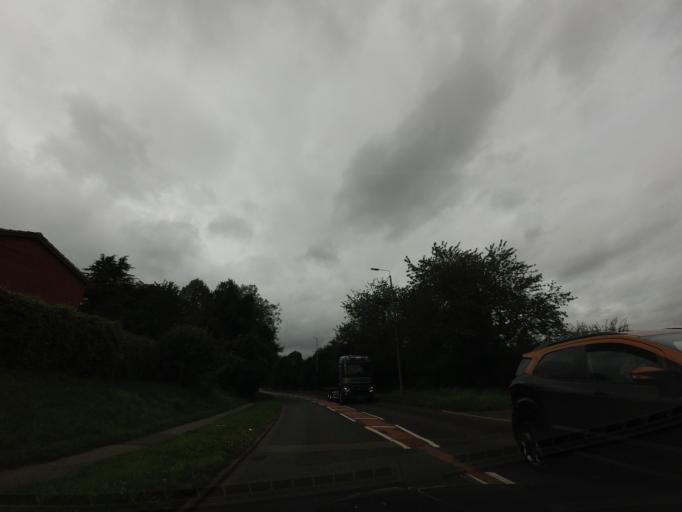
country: GB
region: England
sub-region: Nottinghamshire
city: Kimberley
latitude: 53.0074
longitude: -1.2535
